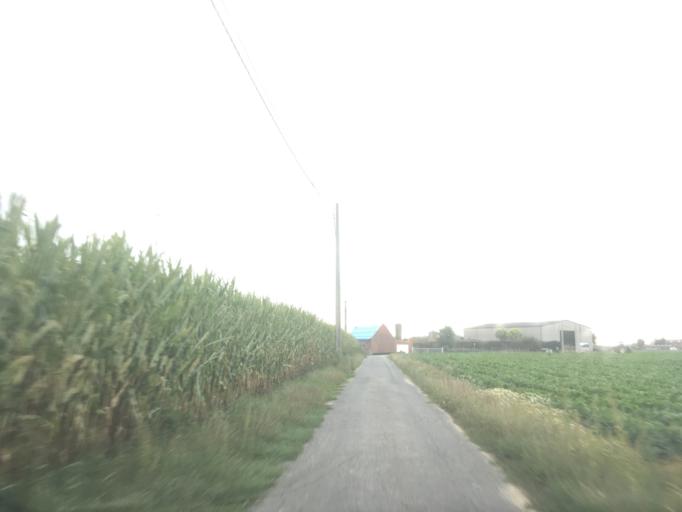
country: BE
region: Flanders
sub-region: Provincie West-Vlaanderen
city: Ardooie
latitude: 51.0186
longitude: 3.2185
